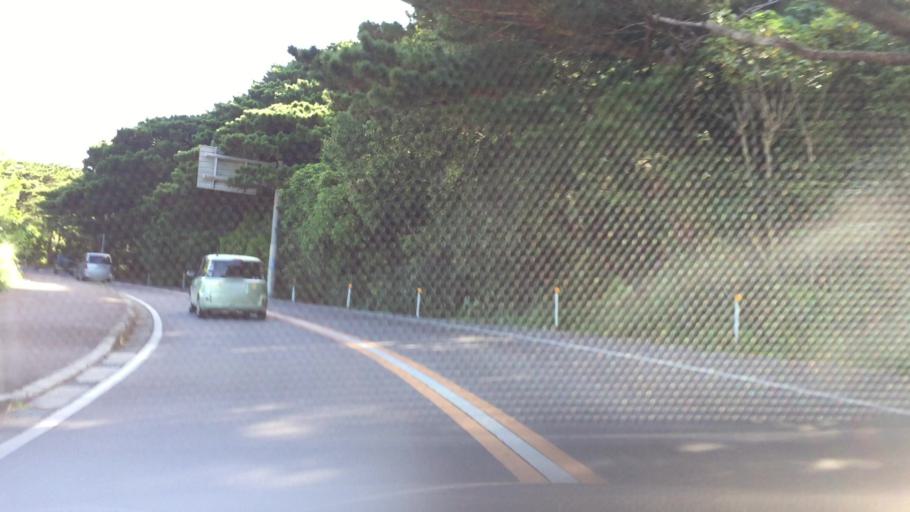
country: JP
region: Okinawa
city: Ishigaki
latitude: 24.4486
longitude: 124.1292
